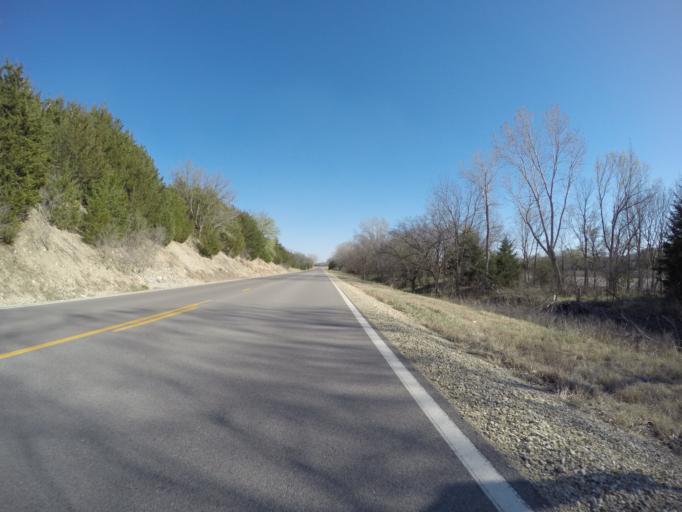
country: US
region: Kansas
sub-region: Riley County
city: Fort Riley North
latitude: 39.2432
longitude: -96.7653
